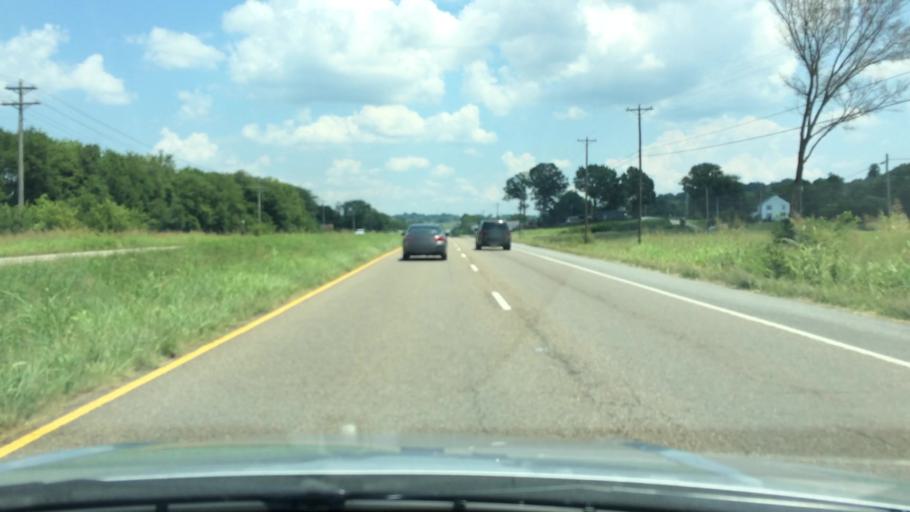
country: US
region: Tennessee
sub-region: Jefferson County
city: New Market
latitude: 36.0952
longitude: -83.5719
